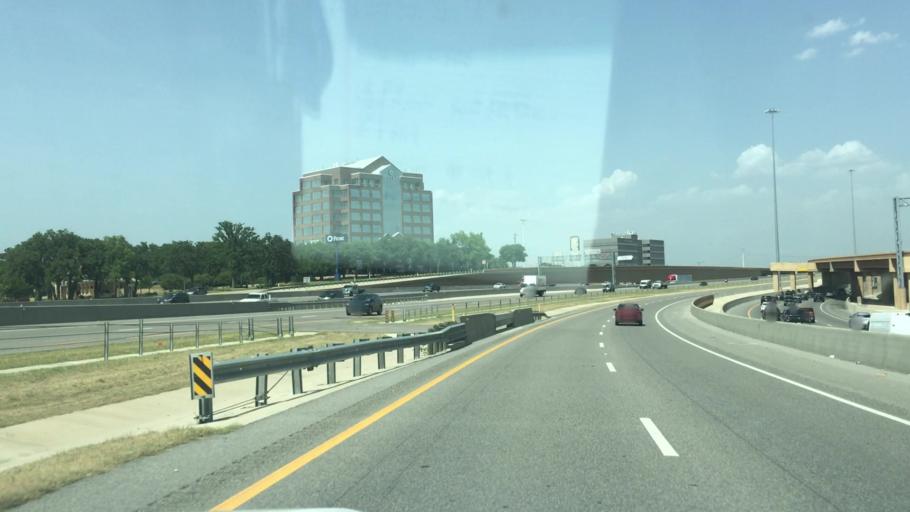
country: US
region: Texas
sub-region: Tarrant County
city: Hurst
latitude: 32.8368
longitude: -97.1956
